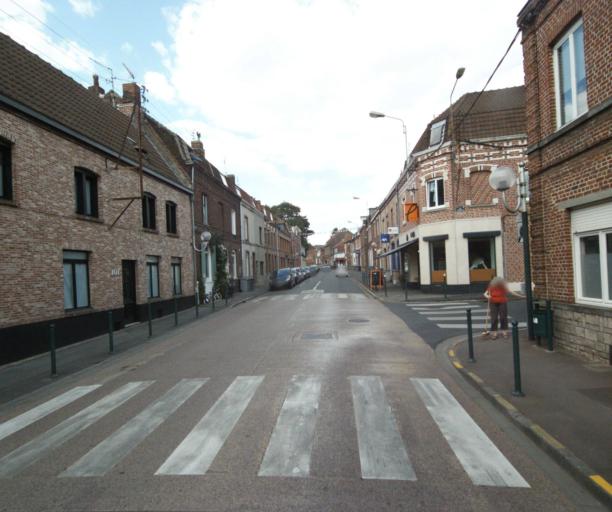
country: FR
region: Nord-Pas-de-Calais
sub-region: Departement du Nord
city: Mouvaux
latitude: 50.6997
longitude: 3.1331
